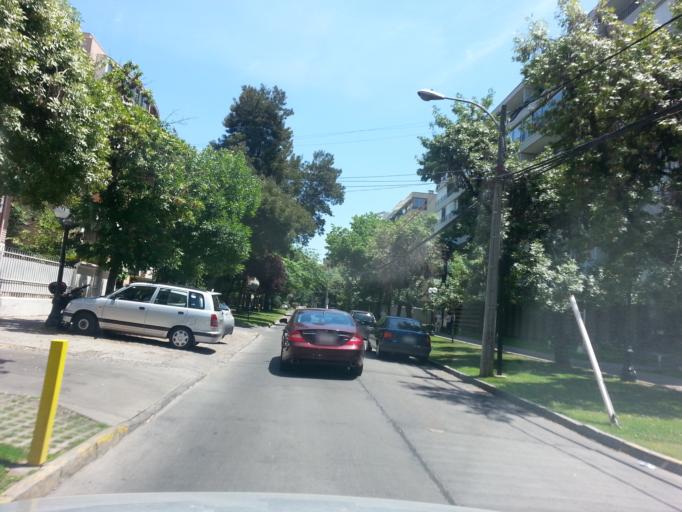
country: CL
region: Santiago Metropolitan
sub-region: Provincia de Santiago
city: Villa Presidente Frei, Nunoa, Santiago, Chile
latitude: -33.4289
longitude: -70.5914
